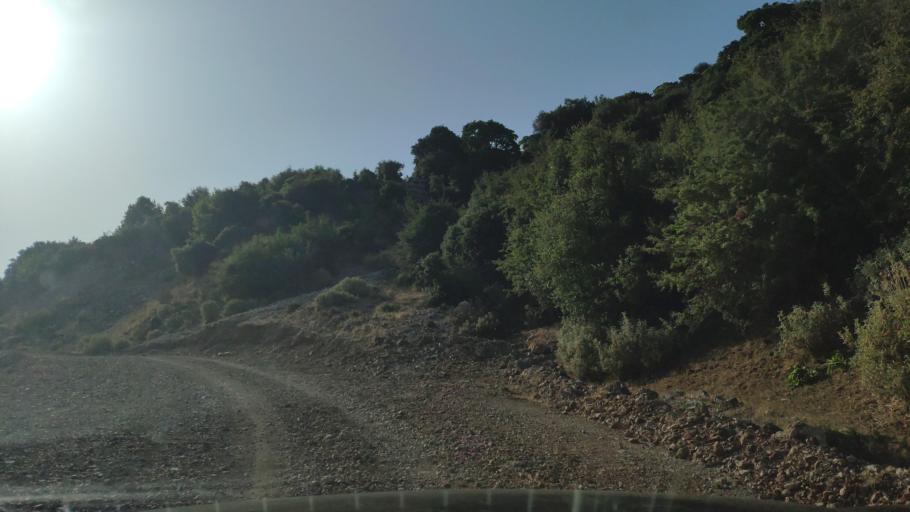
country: GR
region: West Greece
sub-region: Nomos Aitolias kai Akarnanias
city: Monastirakion
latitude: 38.8394
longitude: 20.9720
